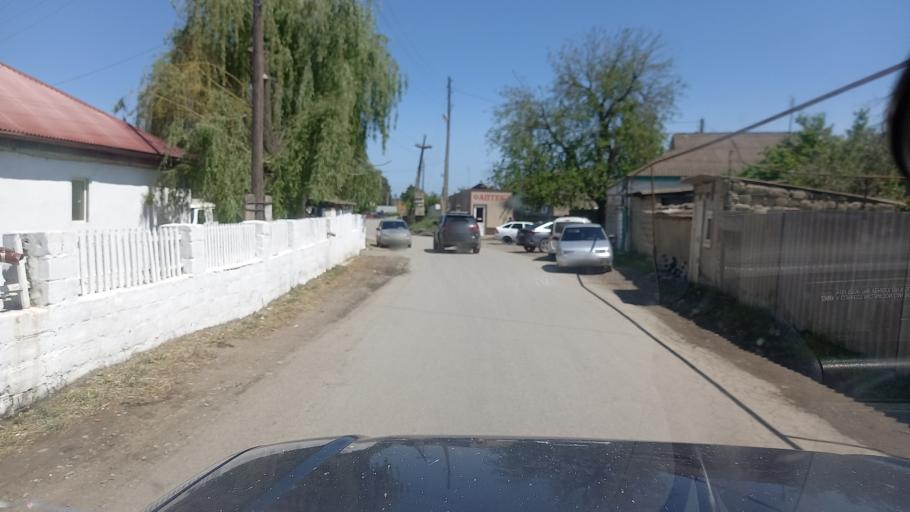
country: RU
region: Dagestan
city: Samur
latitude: 41.8150
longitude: 48.5047
